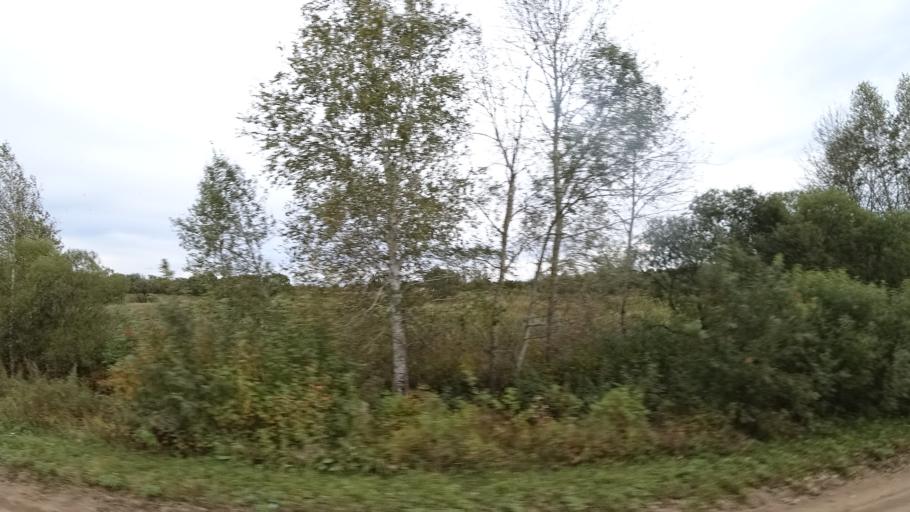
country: RU
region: Amur
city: Arkhara
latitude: 49.4326
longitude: 130.2533
